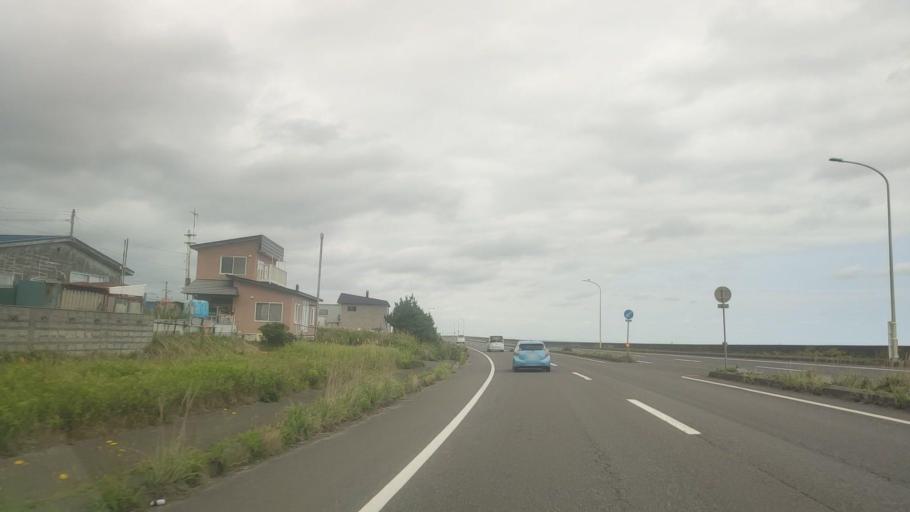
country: JP
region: Hokkaido
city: Shiraoi
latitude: 42.5449
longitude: 141.3545
